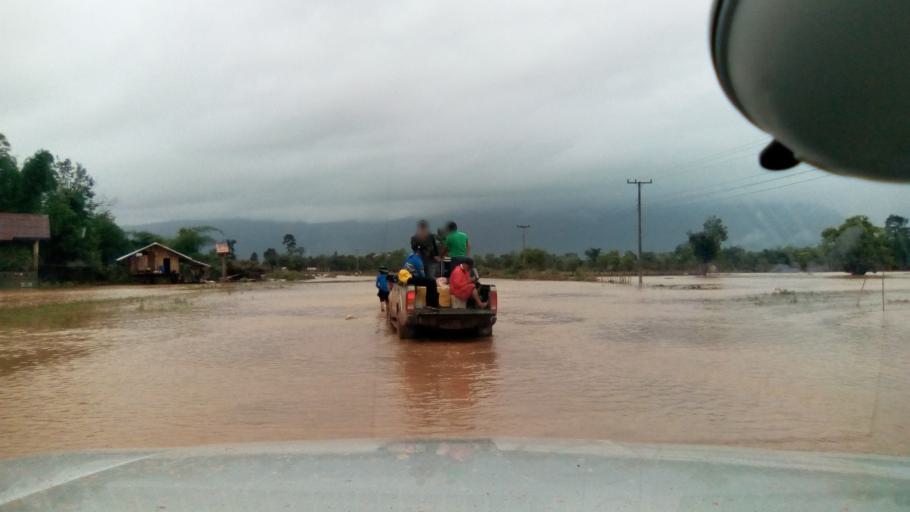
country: LA
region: Attapu
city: Attapu
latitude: 14.6971
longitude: 106.5320
